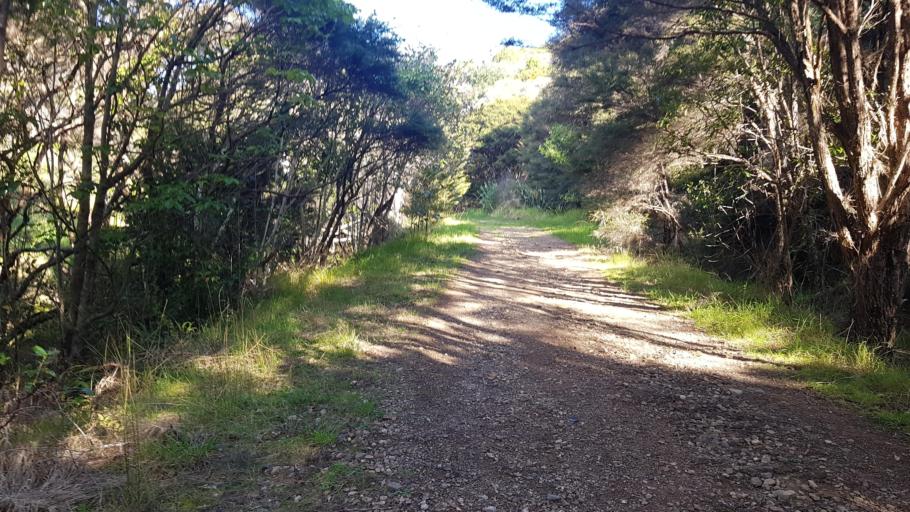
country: NZ
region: Auckland
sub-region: Auckland
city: Pakuranga
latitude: -36.7835
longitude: 174.9968
